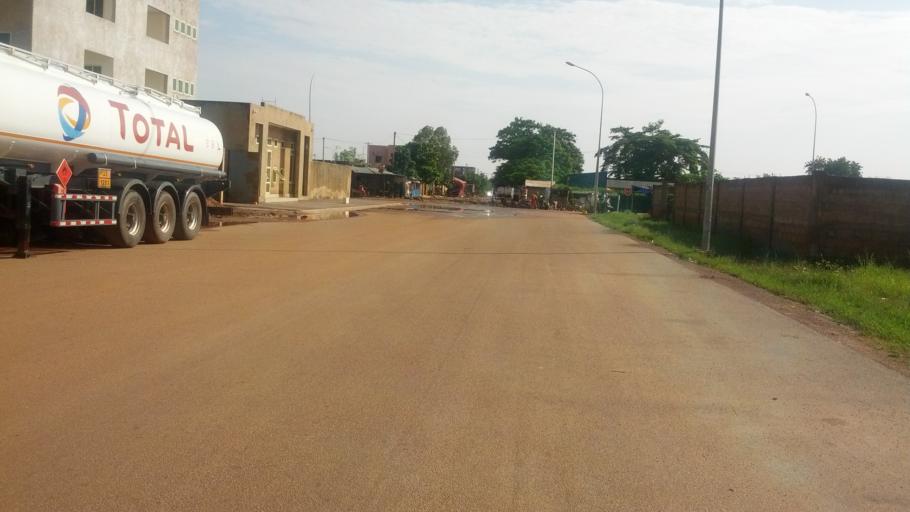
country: BF
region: Centre
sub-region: Kadiogo Province
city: Ouagadougou
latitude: 12.3525
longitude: -1.4919
